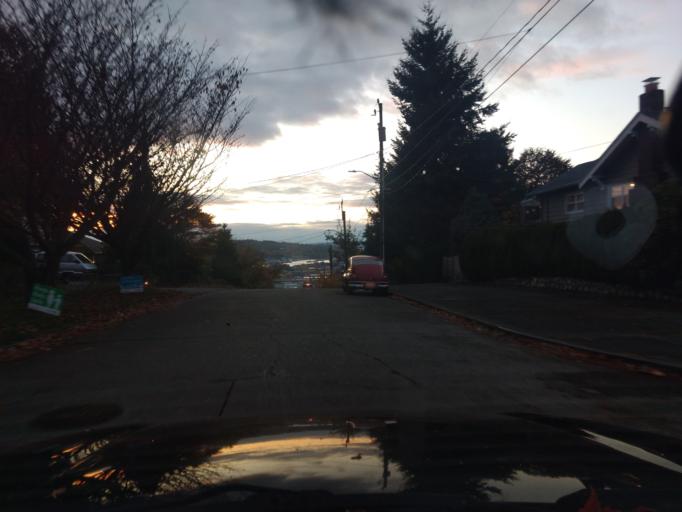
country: US
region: Washington
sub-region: King County
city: Seattle
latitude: 47.6643
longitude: -122.3572
